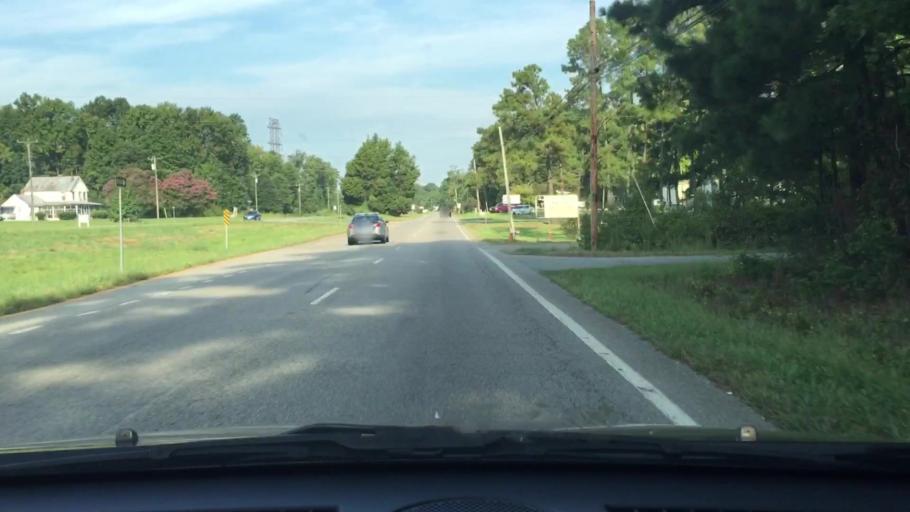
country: US
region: Virginia
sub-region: Isle of Wight County
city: Carrollton
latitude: 36.9416
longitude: -76.5455
